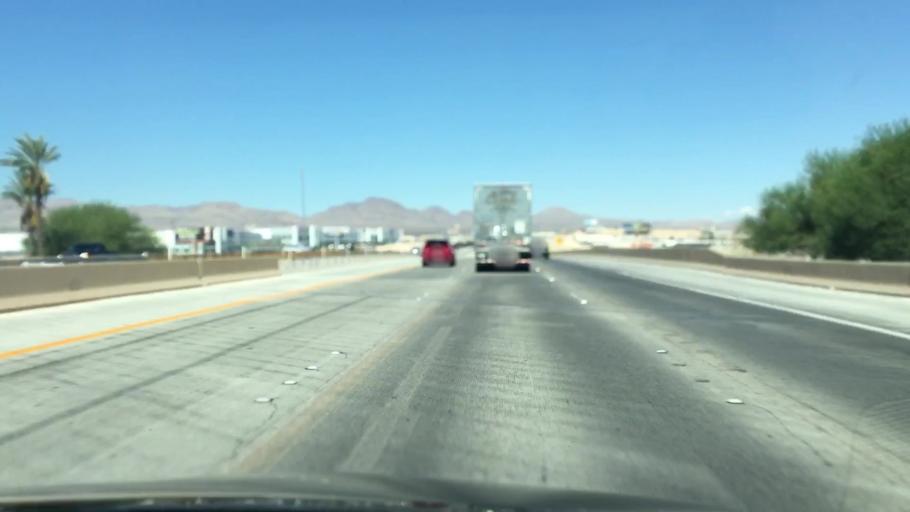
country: US
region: Nevada
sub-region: Clark County
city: Nellis Air Force Base
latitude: 36.2583
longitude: -115.0792
